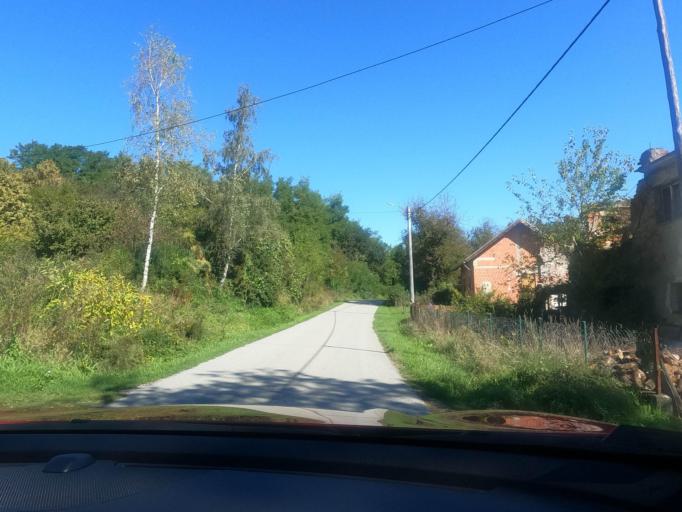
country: HR
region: Sisacko-Moslavacka
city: Petrinja
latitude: 45.3800
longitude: 16.2413
